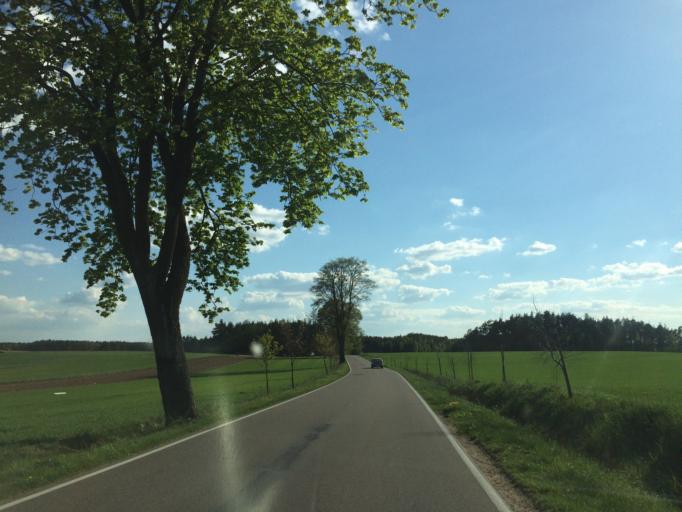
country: PL
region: Warmian-Masurian Voivodeship
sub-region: Powiat dzialdowski
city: Lidzbark
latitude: 53.2891
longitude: 19.8553
